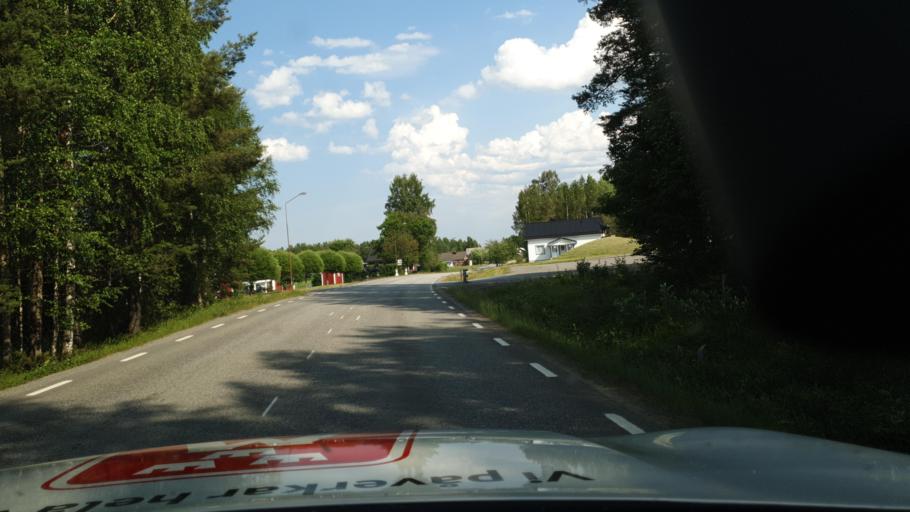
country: SE
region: Vaesterbotten
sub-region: Skelleftea Kommun
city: Viken
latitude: 64.7502
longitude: 20.8843
